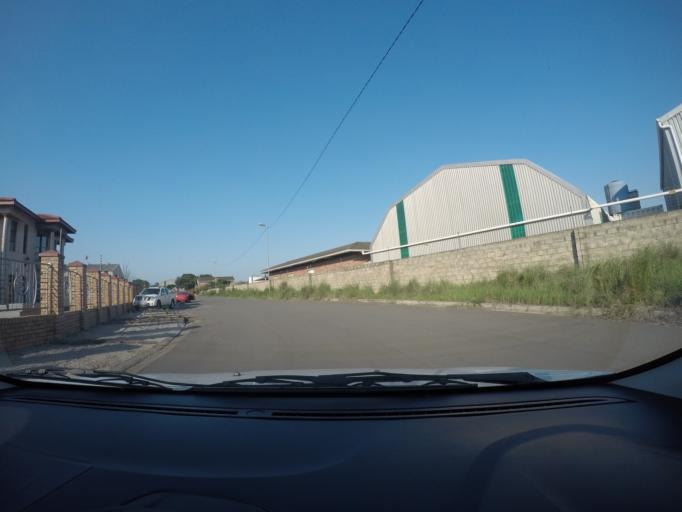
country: ZA
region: KwaZulu-Natal
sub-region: uThungulu District Municipality
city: Richards Bay
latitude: -28.7515
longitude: 32.0162
